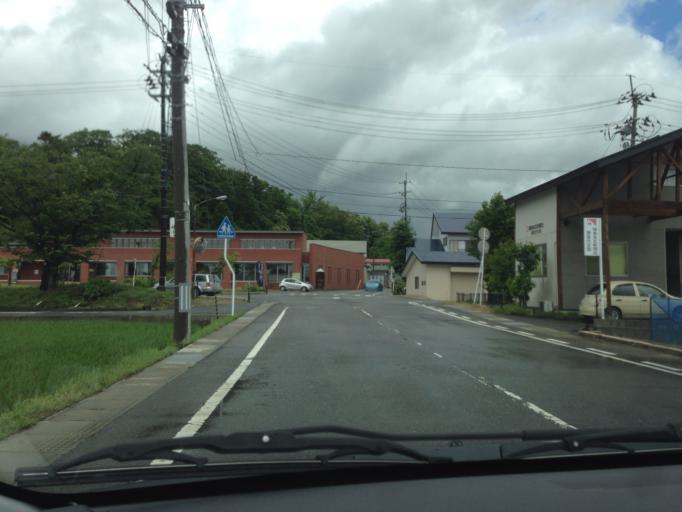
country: JP
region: Fukushima
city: Inawashiro
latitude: 37.5596
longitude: 140.1043
